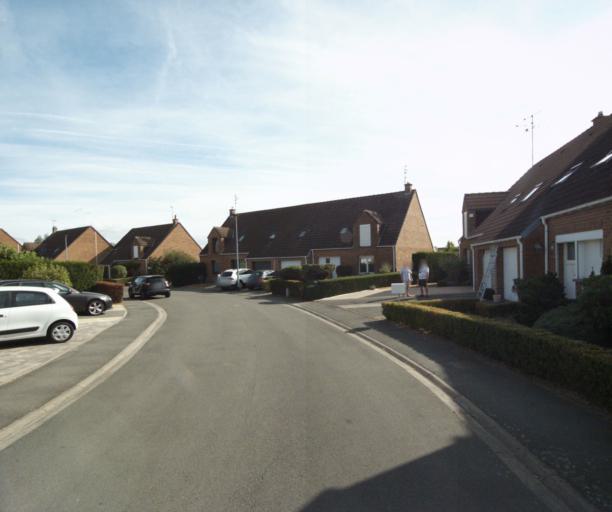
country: FR
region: Nord-Pas-de-Calais
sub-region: Departement du Nord
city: Linselles
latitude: 50.7353
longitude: 3.0872
